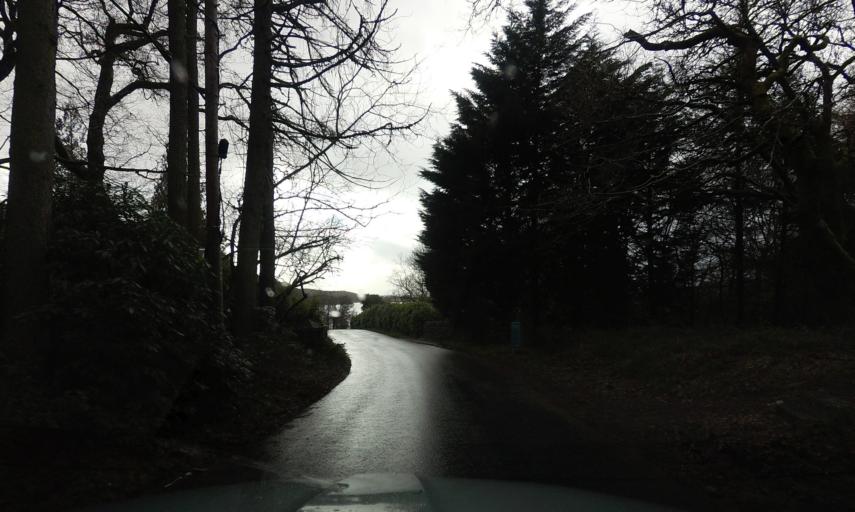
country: GB
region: Scotland
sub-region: West Dunbartonshire
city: Balloch
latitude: 56.1210
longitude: -4.5921
